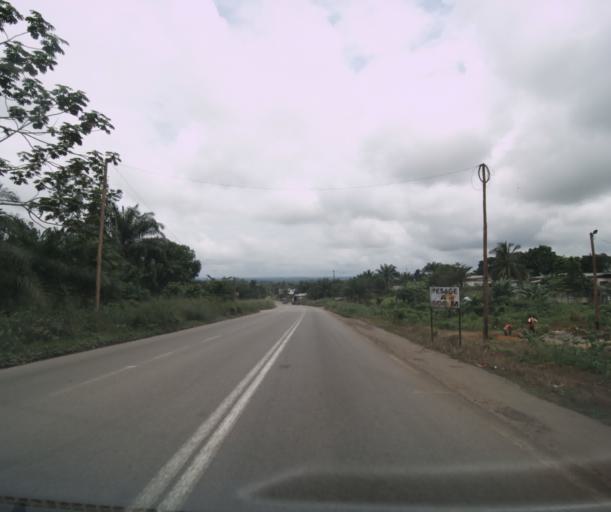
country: CM
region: Littoral
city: Edea
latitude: 3.7856
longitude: 10.1502
